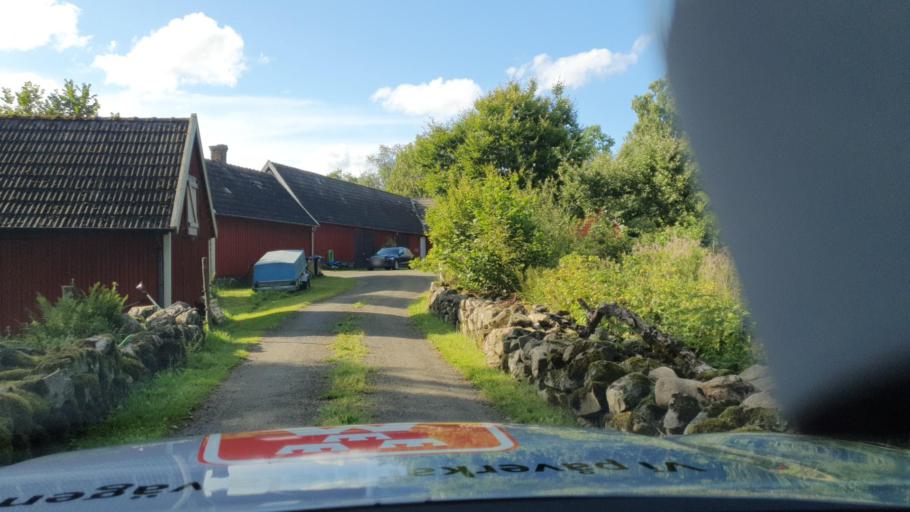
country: SE
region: Skane
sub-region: Hassleholms Kommun
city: Vinslov
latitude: 56.0431
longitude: 13.8678
